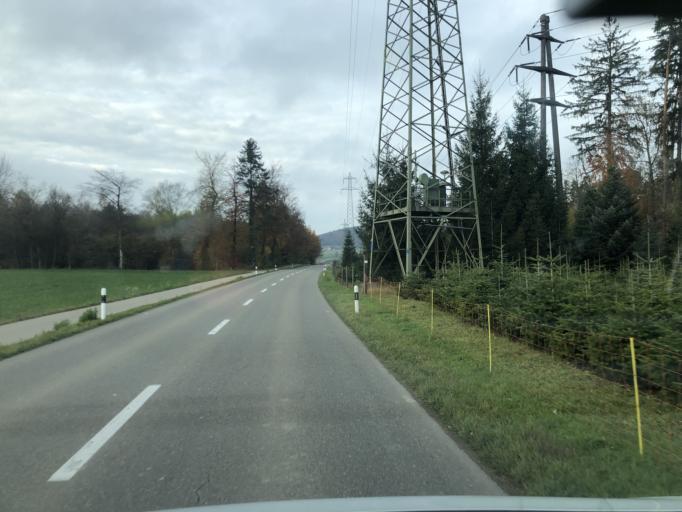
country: CH
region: Aargau
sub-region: Bezirk Baden
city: Mellingen
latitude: 47.4450
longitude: 8.2788
